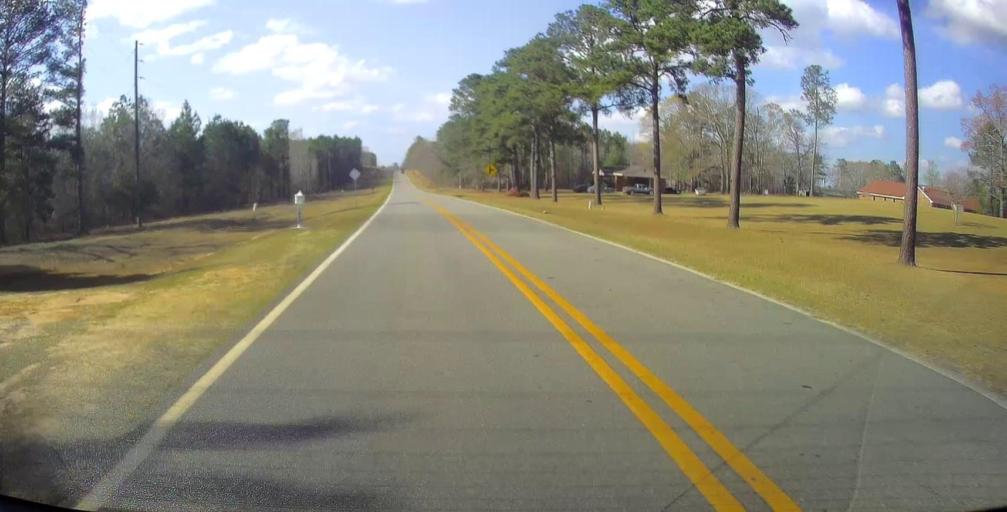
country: US
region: Georgia
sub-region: Laurens County
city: Dublin
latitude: 32.6187
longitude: -83.0868
